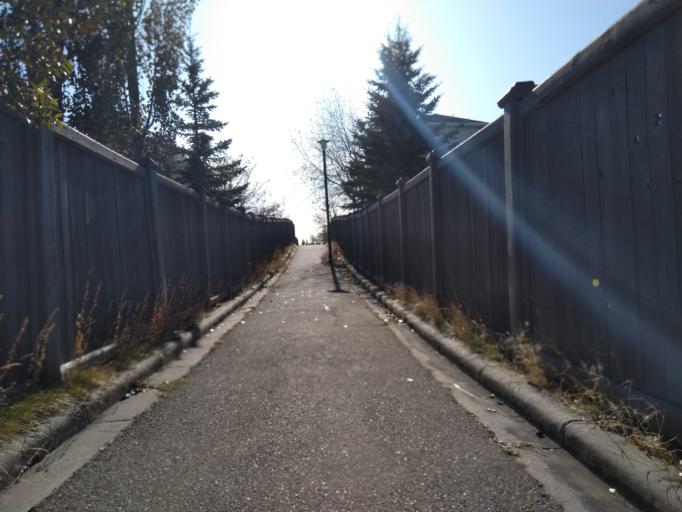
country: CA
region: Alberta
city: Calgary
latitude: 51.1482
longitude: -114.1150
